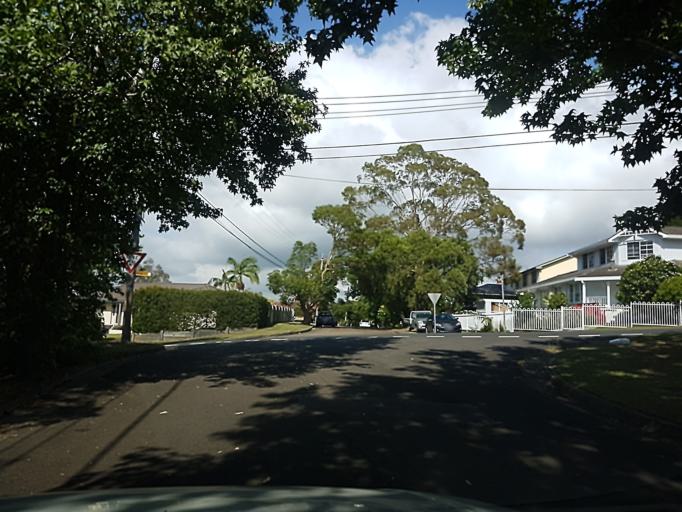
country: AU
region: New South Wales
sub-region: Warringah
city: Davidson
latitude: -33.7462
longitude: 151.2065
